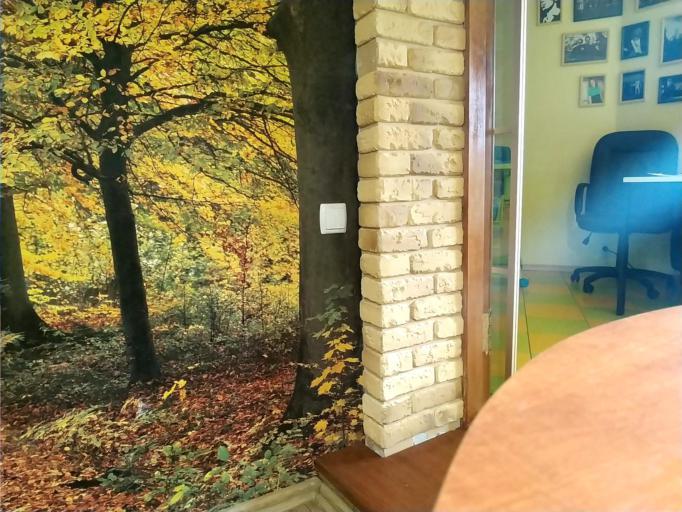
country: BY
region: Mogilev
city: Khotsimsk
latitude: 53.5651
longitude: 32.5381
